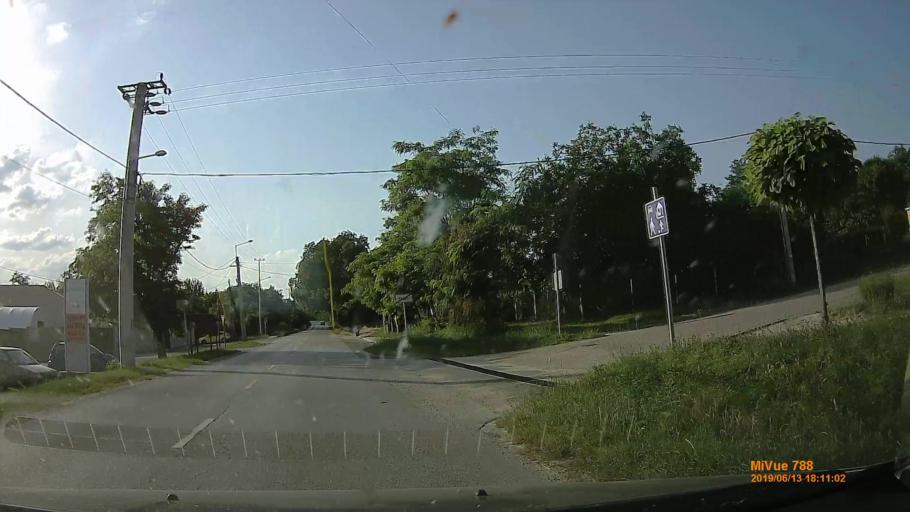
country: HU
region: Pest
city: Ecser
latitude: 47.4516
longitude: 19.3053
